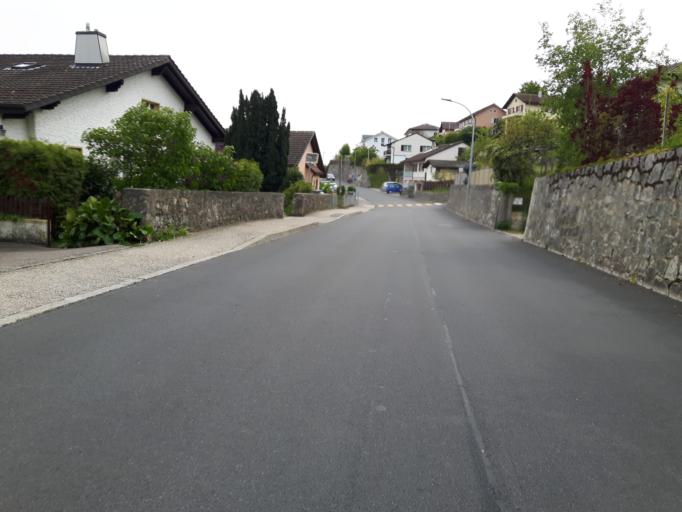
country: CH
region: Neuchatel
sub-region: Boudry District
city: Gorgier
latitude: 46.9007
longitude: 6.7791
